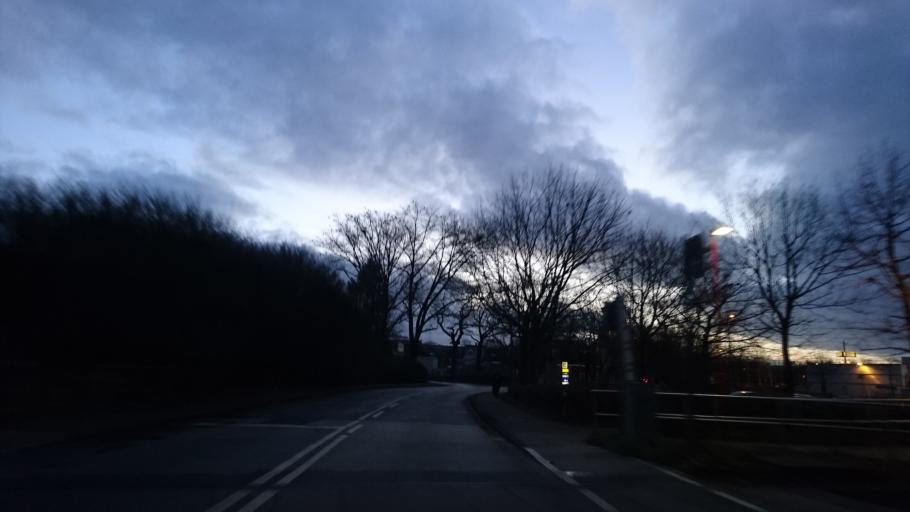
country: DE
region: Hamburg
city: Eidelstedt
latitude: 53.6180
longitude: 9.9037
